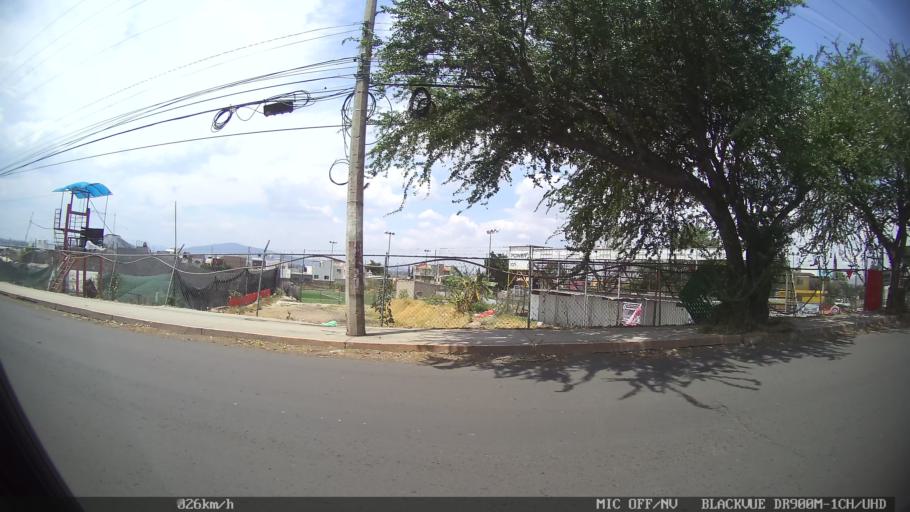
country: MX
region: Jalisco
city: Tlaquepaque
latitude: 20.6344
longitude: -103.2720
